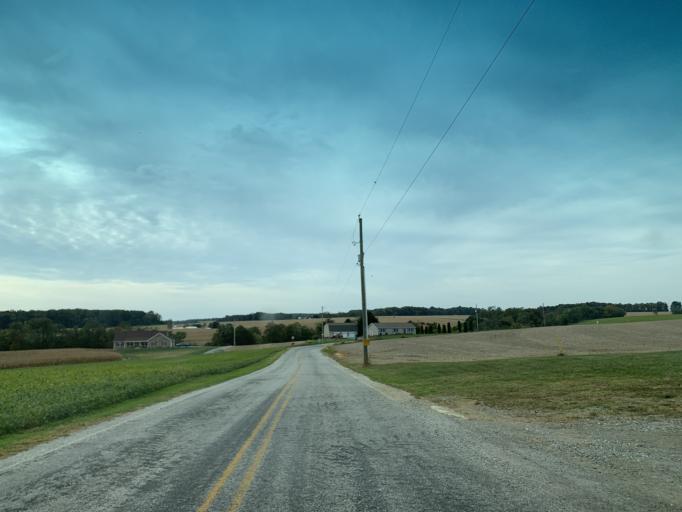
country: US
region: Pennsylvania
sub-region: York County
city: Stewartstown
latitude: 39.8033
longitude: -76.5130
